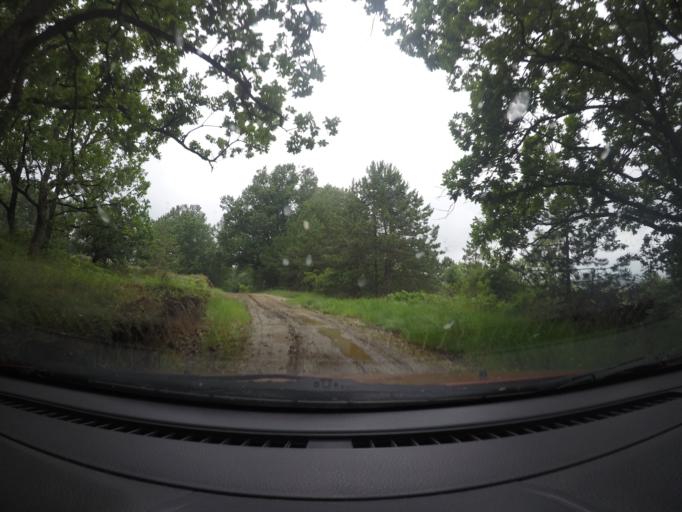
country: RS
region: Central Serbia
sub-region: Belgrade
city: Sopot
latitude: 44.5463
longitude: 20.5093
